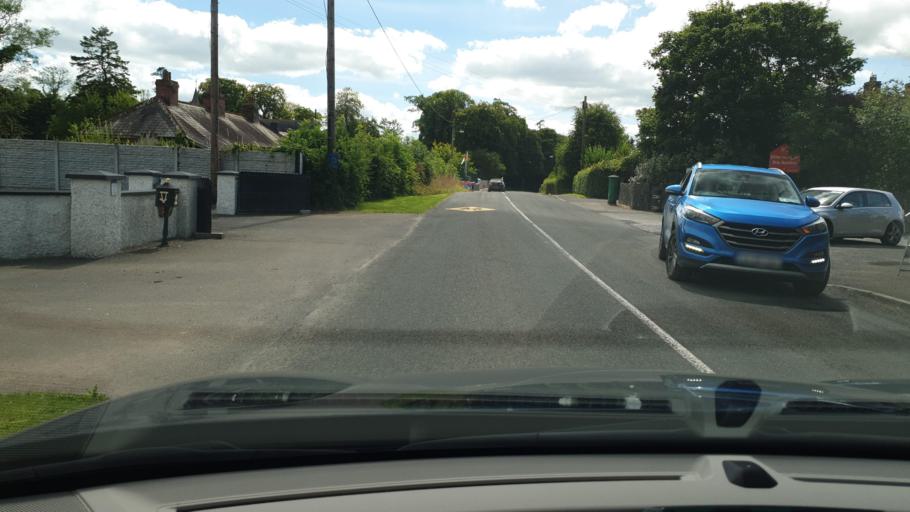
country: IE
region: Leinster
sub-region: An Mhi
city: Dunshaughlin
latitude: 53.5450
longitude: -6.6172
